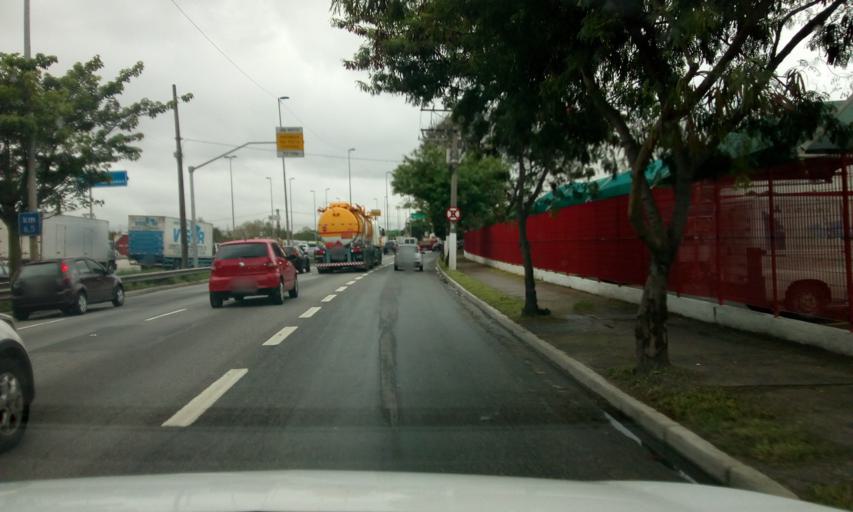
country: BR
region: Sao Paulo
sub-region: Sao Paulo
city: Sao Paulo
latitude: -23.5089
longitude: -46.6959
